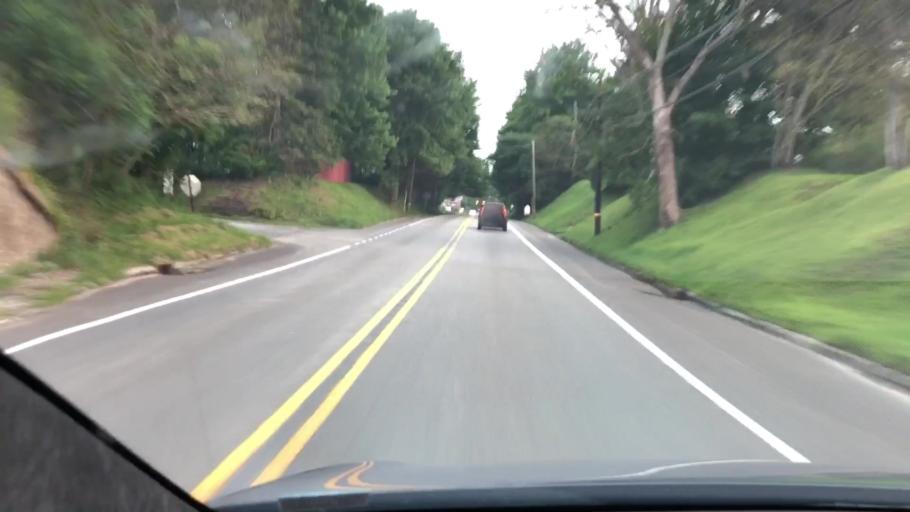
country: US
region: Pennsylvania
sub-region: Butler County
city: Slippery Rock
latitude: 41.1094
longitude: -80.0063
